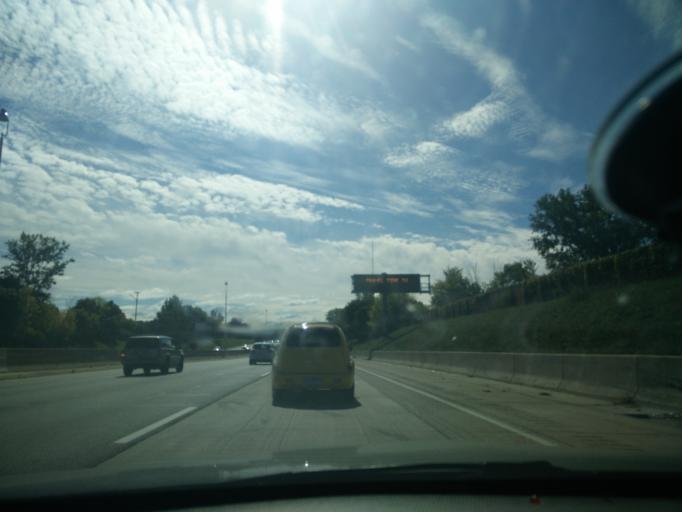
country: US
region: Michigan
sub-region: Macomb County
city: Roseville
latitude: 42.4893
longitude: -82.9173
